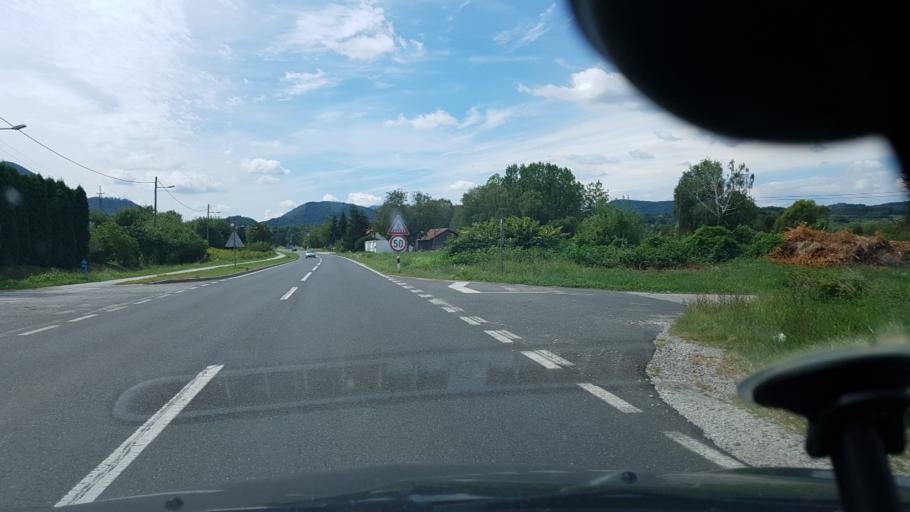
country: HR
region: Varazdinska
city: Lepoglava
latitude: 46.2135
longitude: 16.0469
